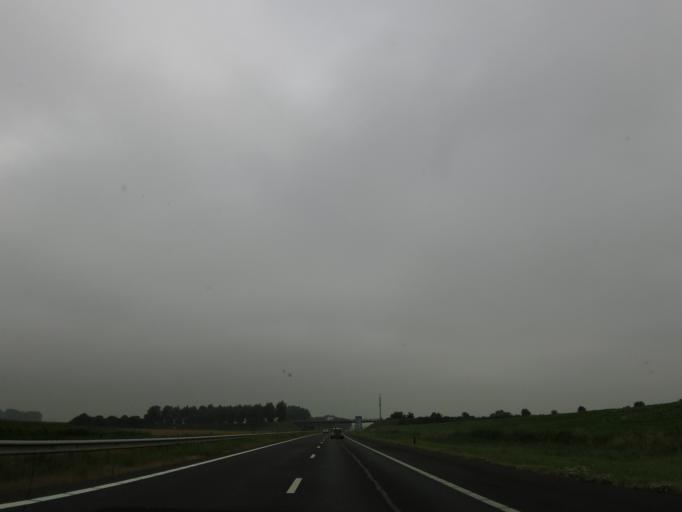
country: NL
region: North Brabant
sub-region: Gemeente Woensdrecht
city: Woensdrecht
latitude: 51.3910
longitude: 4.2937
